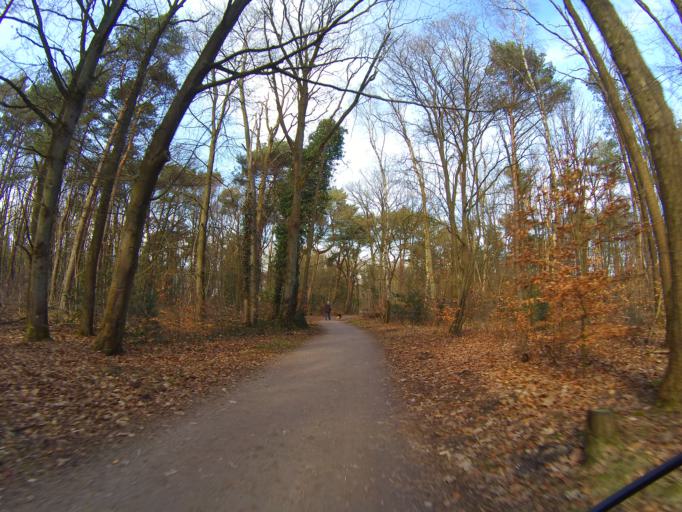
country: NL
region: North Holland
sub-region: Gemeente Hilversum
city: Hilversum
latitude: 52.2379
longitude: 5.1996
